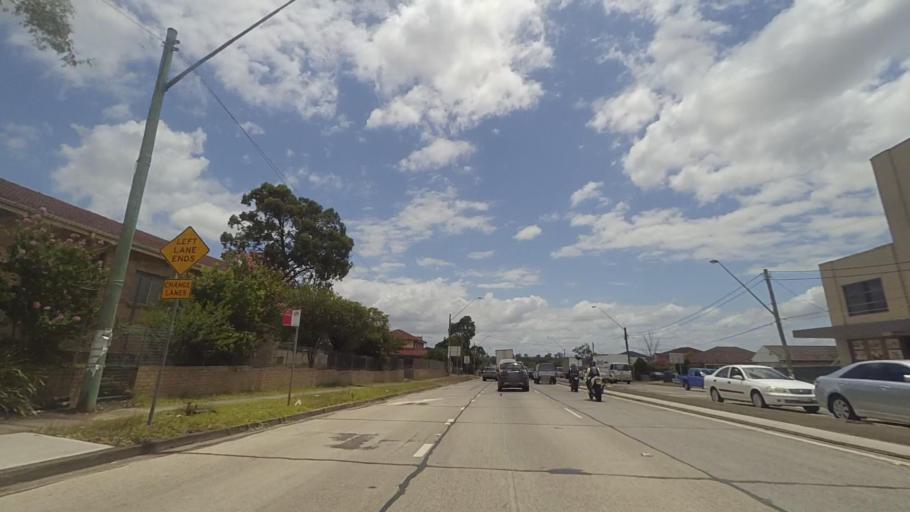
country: AU
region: New South Wales
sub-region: Fairfield
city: Cabramatta West
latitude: -33.8835
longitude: 150.9238
